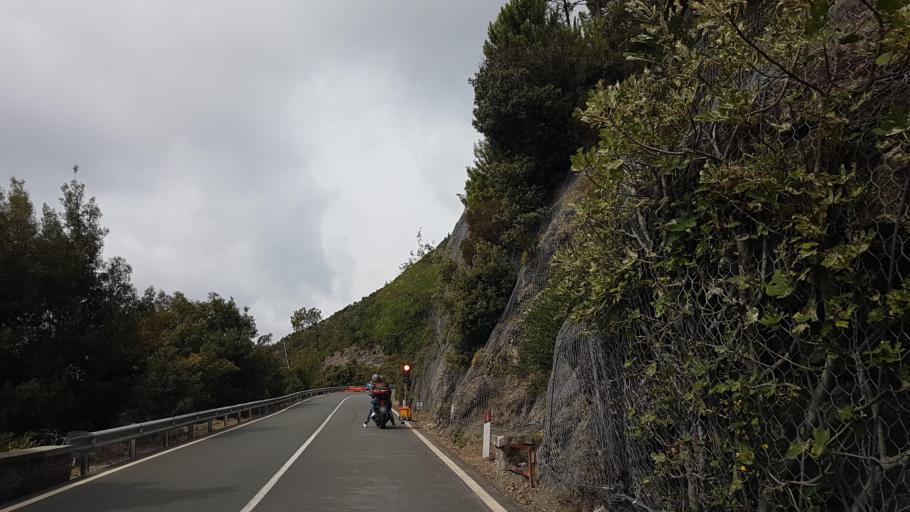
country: IT
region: Liguria
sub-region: Provincia di La Spezia
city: Framura
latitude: 44.2511
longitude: 9.5675
